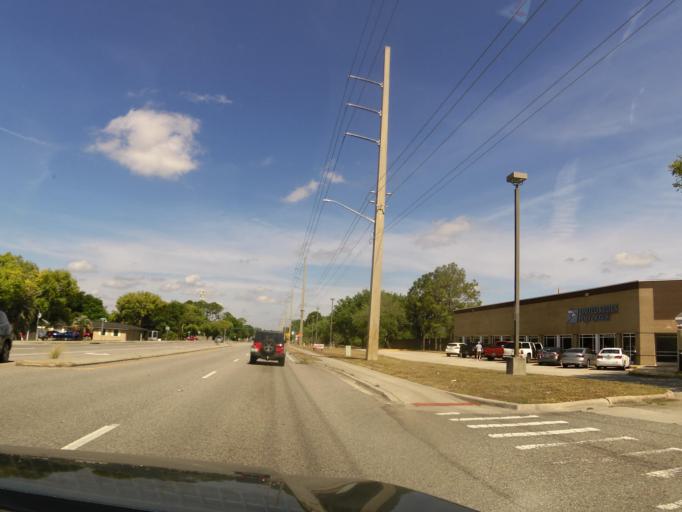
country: US
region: Florida
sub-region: Volusia County
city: Lake Helen
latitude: 28.9212
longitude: -81.1855
